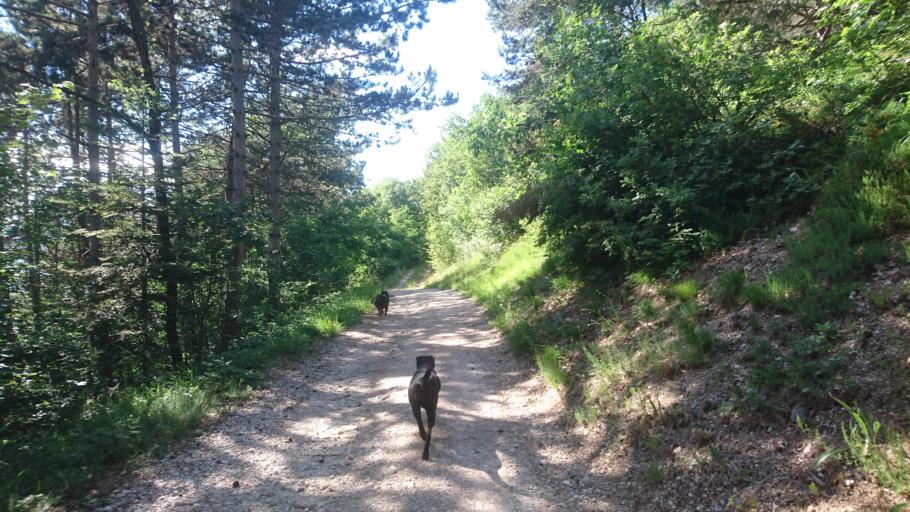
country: IT
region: Trentino-Alto Adige
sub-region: Provincia di Trento
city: Drena
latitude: 45.9726
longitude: 10.9591
